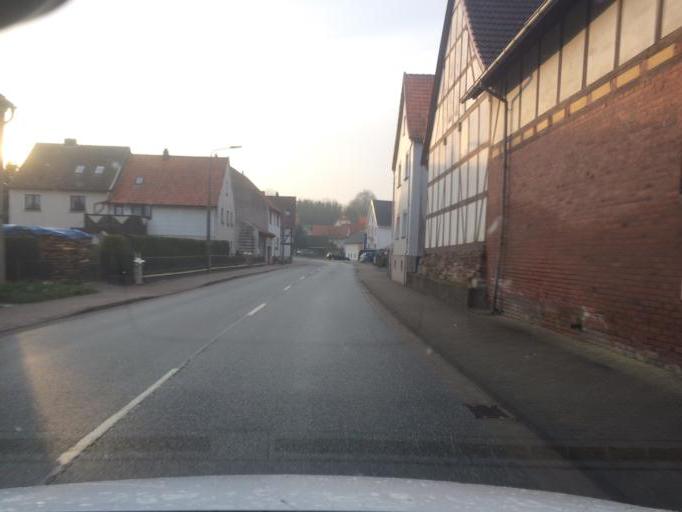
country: DE
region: Thuringia
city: Weissenborn-Luderode
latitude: 51.5288
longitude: 10.4295
